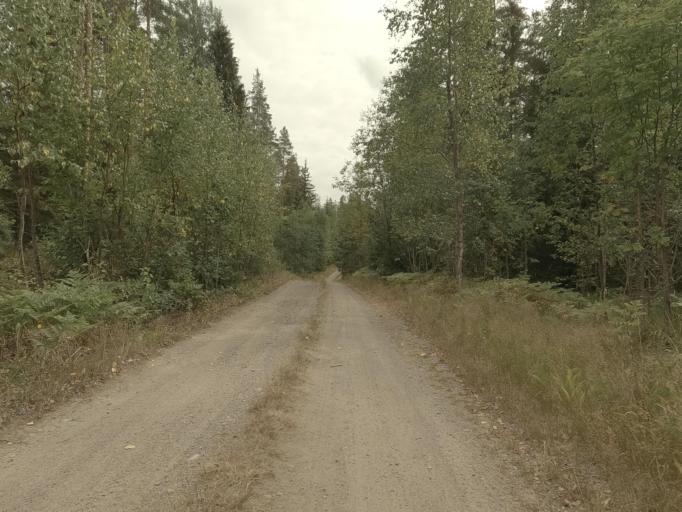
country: RU
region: Leningrad
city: Kamennogorsk
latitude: 61.0195
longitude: 29.1905
